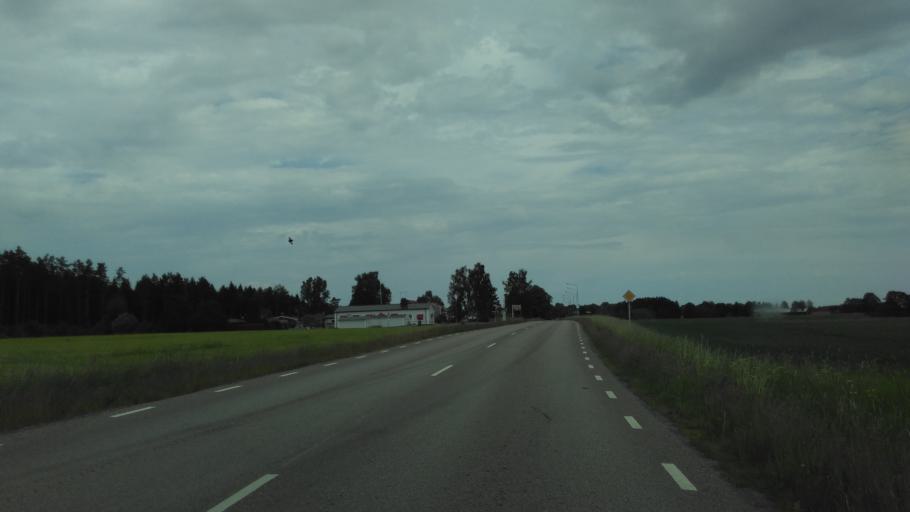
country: SE
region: Vaestra Goetaland
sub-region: Lidkopings Kommun
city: Lidkoping
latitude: 58.4321
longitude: 13.1588
